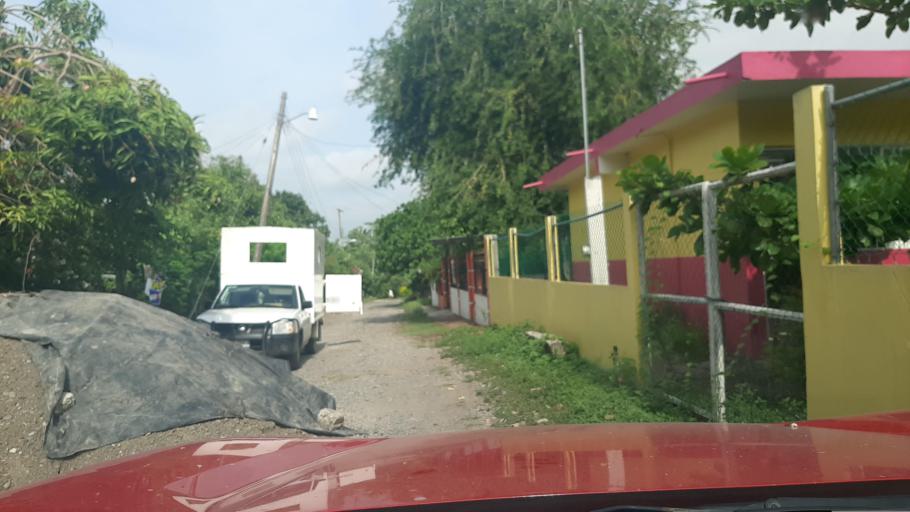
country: MX
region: Veracruz
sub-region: Coatzintla
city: Corralillos
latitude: 20.4850
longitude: -97.5019
